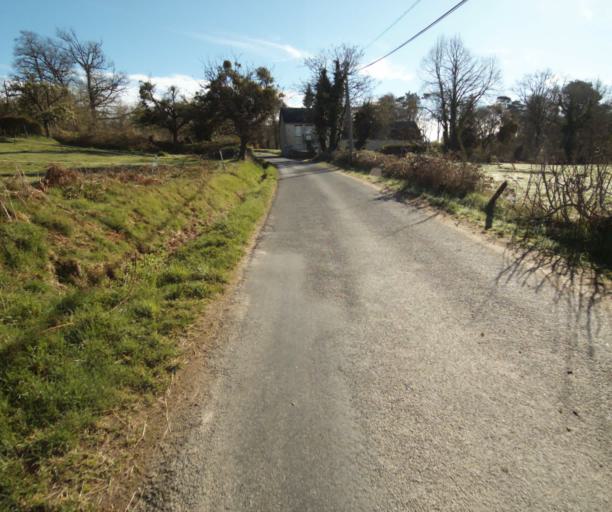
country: FR
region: Limousin
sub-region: Departement de la Correze
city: Correze
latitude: 45.2681
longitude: 1.8844
